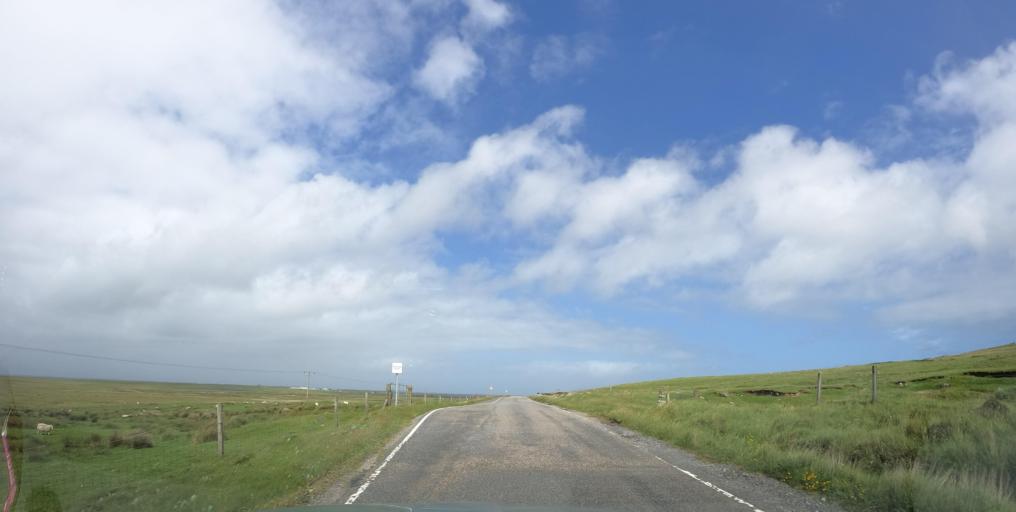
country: GB
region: Scotland
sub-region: Eilean Siar
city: Isle of South Uist
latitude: 57.3416
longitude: -7.3646
